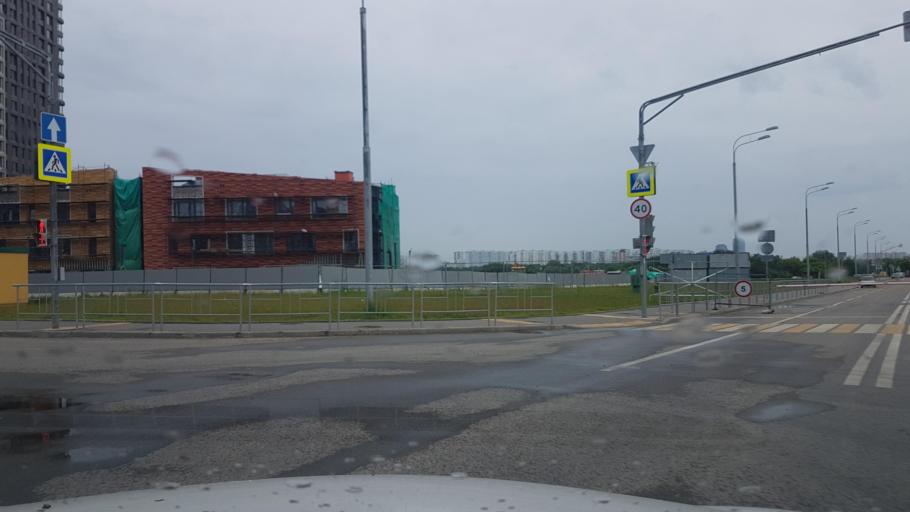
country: RU
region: Moscow
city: Strogino
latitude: 55.8219
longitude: 37.4237
